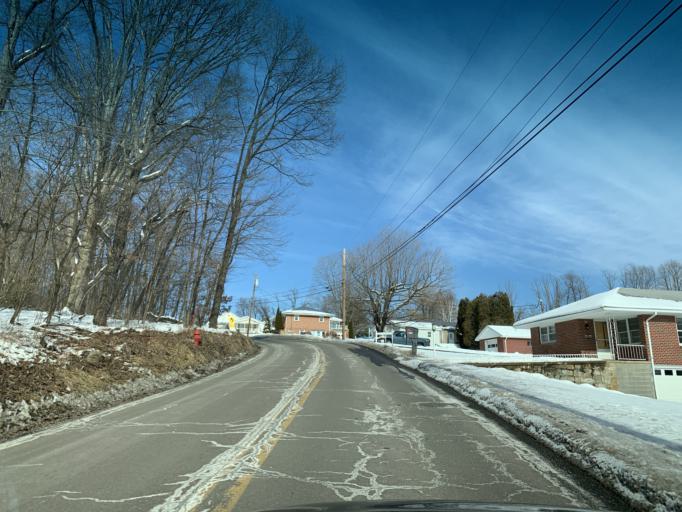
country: US
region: Maryland
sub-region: Allegany County
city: Frostburg
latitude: 39.6616
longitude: -78.8895
